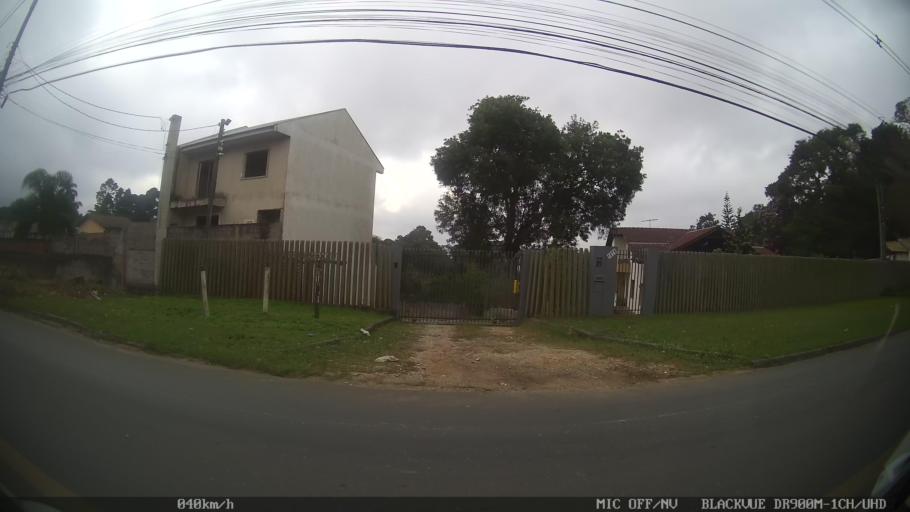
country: BR
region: Parana
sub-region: Almirante Tamandare
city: Almirante Tamandare
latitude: -25.3630
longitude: -49.2716
